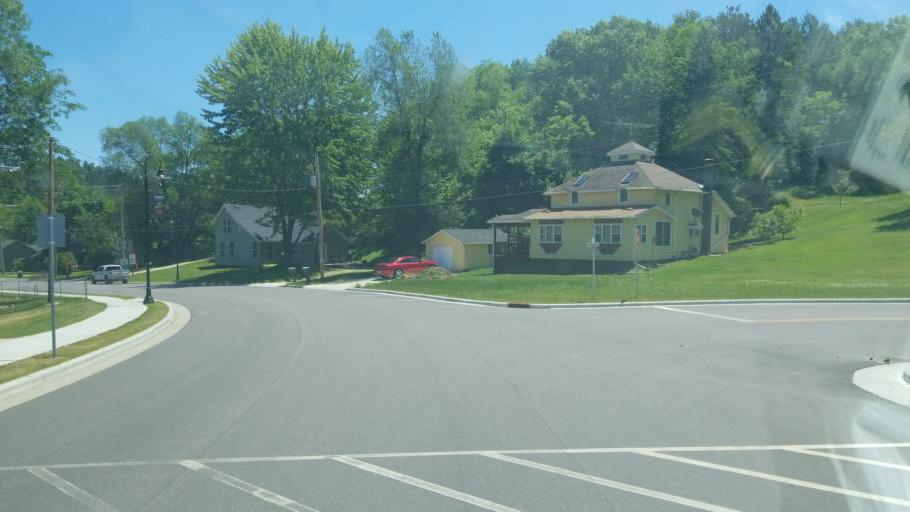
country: US
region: Wisconsin
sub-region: Juneau County
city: New Lisbon
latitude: 43.9207
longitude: -90.2716
